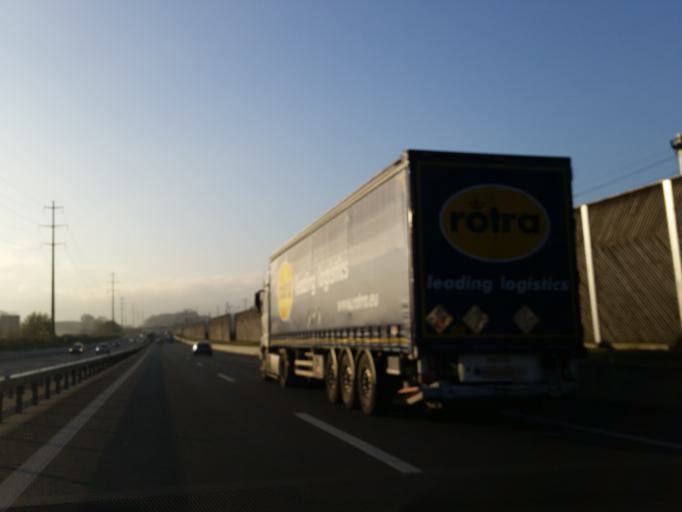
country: CH
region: Zurich
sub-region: Bezirk Affoltern
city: Knonau
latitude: 47.2242
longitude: 8.4651
